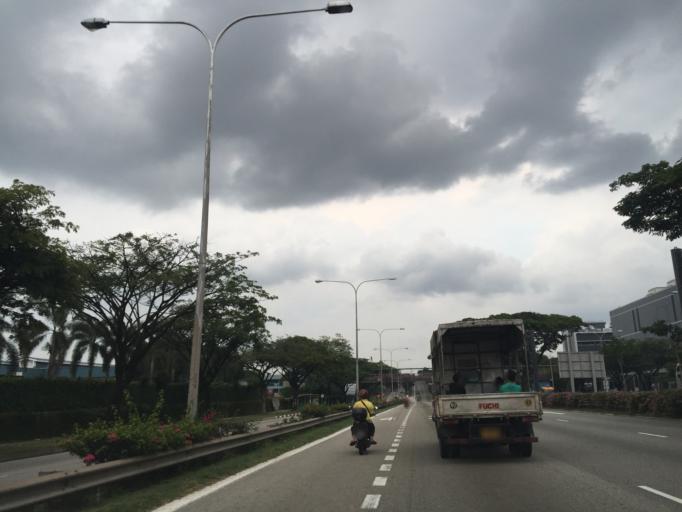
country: SG
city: Singapore
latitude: 1.3224
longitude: 103.7016
